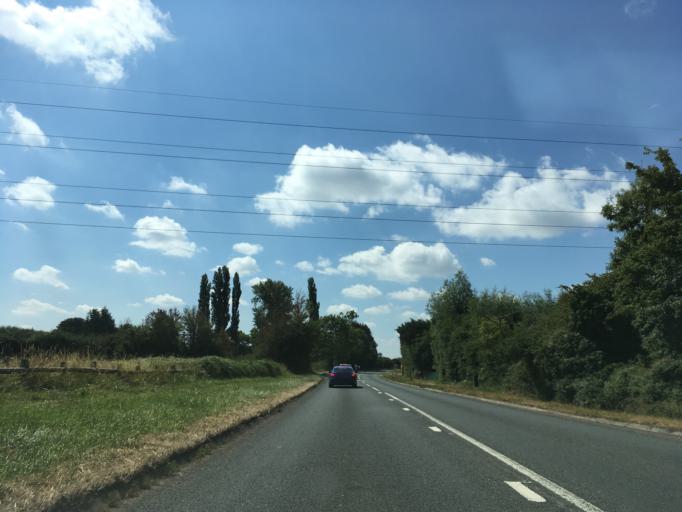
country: GB
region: England
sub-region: Gloucestershire
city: Barnwood
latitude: 51.9115
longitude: -2.2121
